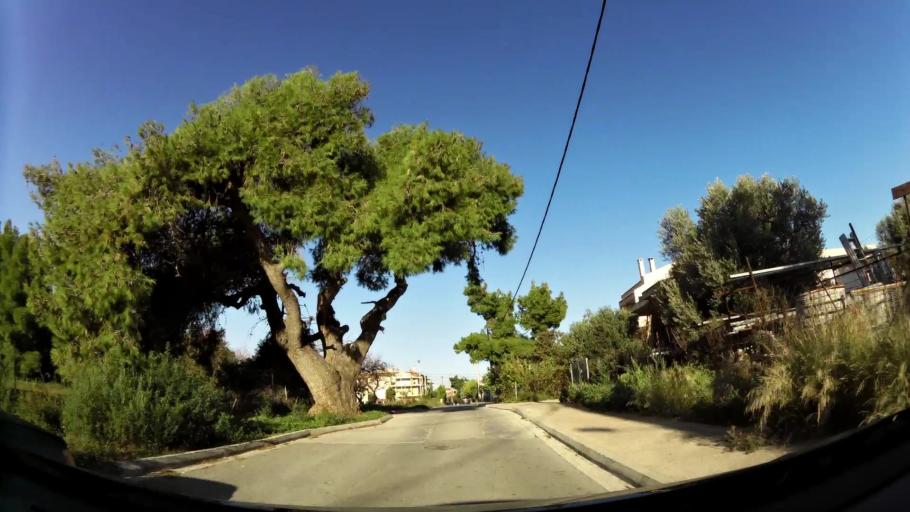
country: GR
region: Attica
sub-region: Nomarchia Athinas
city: Vrilissia
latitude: 38.0304
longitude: 23.8421
